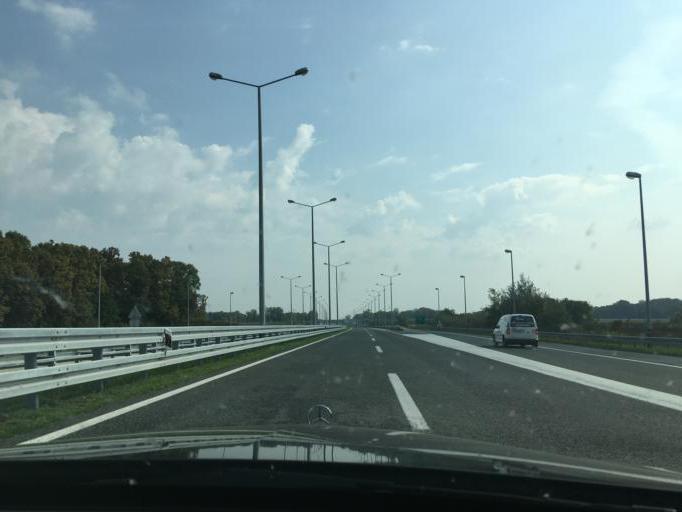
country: HR
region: Brodsko-Posavska
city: Vrpolje
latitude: 45.1449
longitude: 18.3016
